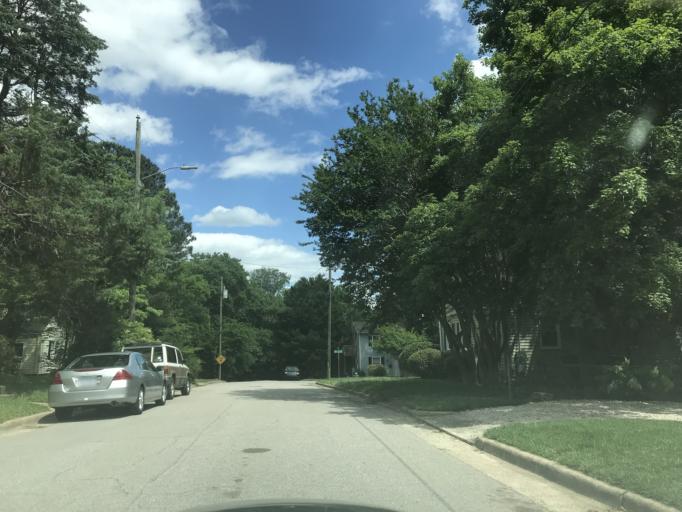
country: US
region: North Carolina
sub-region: Wake County
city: Raleigh
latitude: 35.8058
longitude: -78.6260
